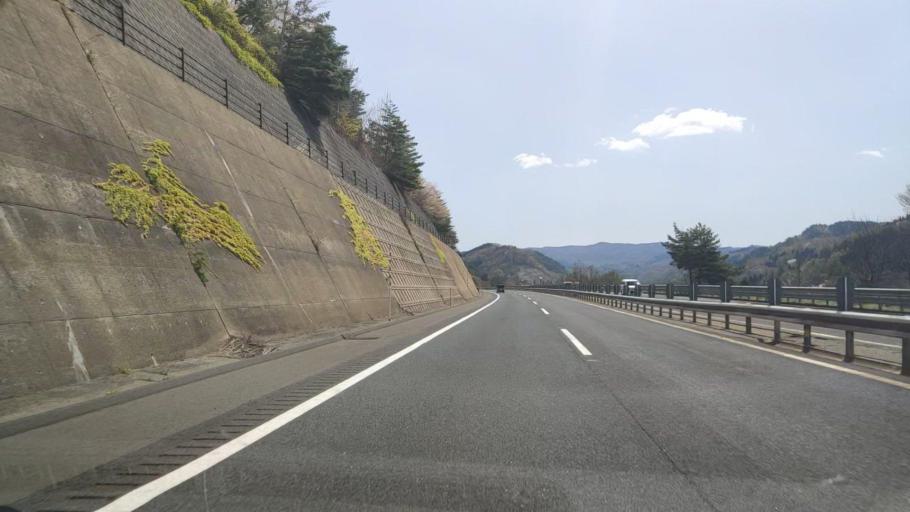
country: JP
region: Iwate
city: Ichinohe
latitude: 40.2307
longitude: 141.3137
